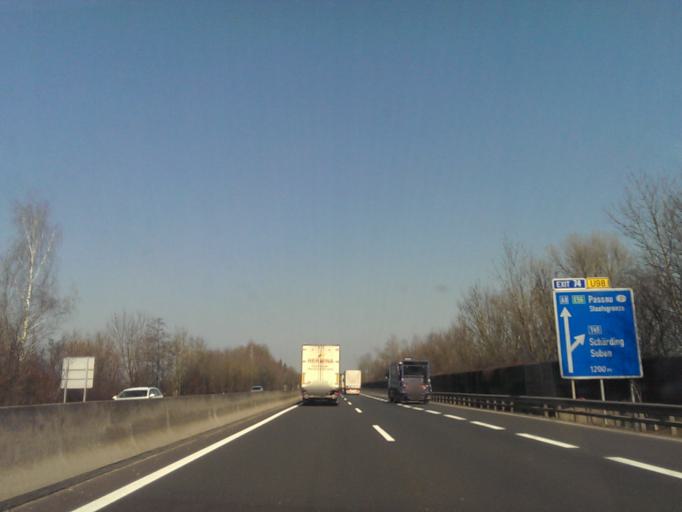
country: AT
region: Upper Austria
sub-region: Politischer Bezirk Scharding
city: Sankt Marienkirchen bei Schaerding
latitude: 48.3785
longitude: 13.4170
